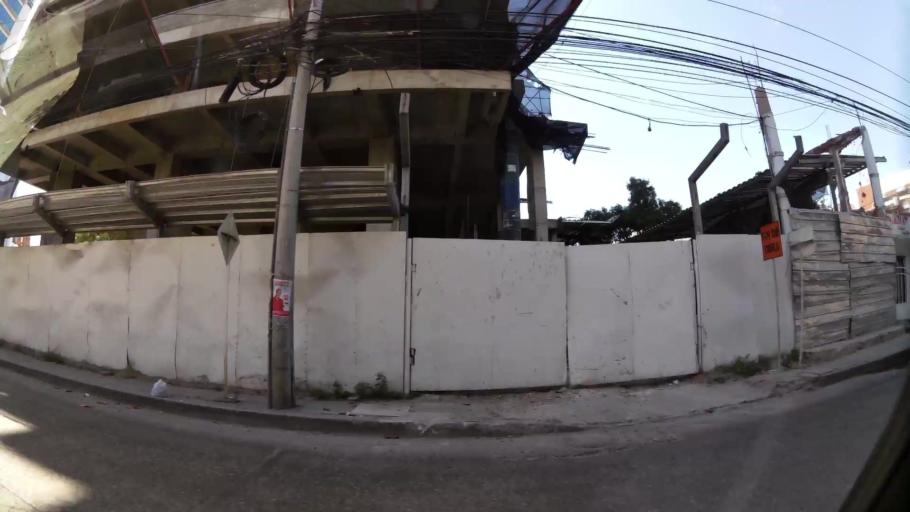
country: CO
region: Bolivar
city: Cartagena
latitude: 10.4099
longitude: -75.5325
